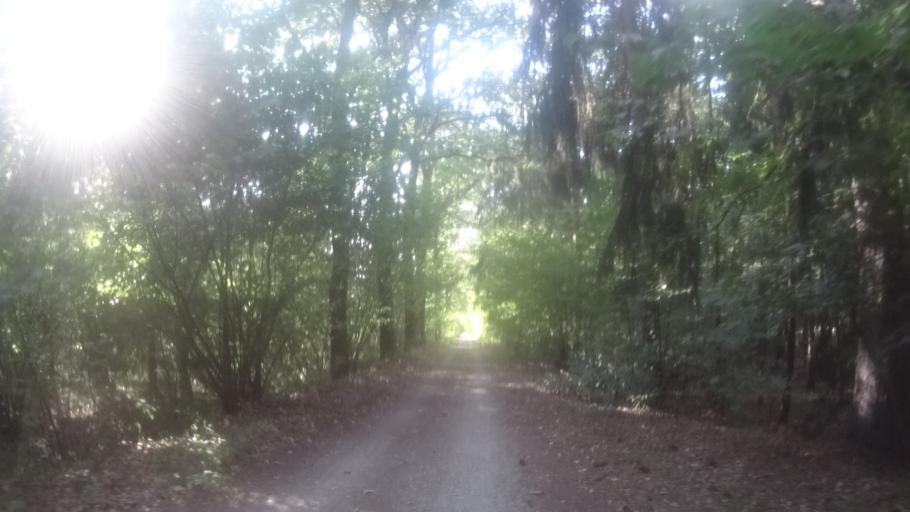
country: CZ
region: Kralovehradecky
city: Trebechovice pod Orebem
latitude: 50.1858
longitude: 16.0131
